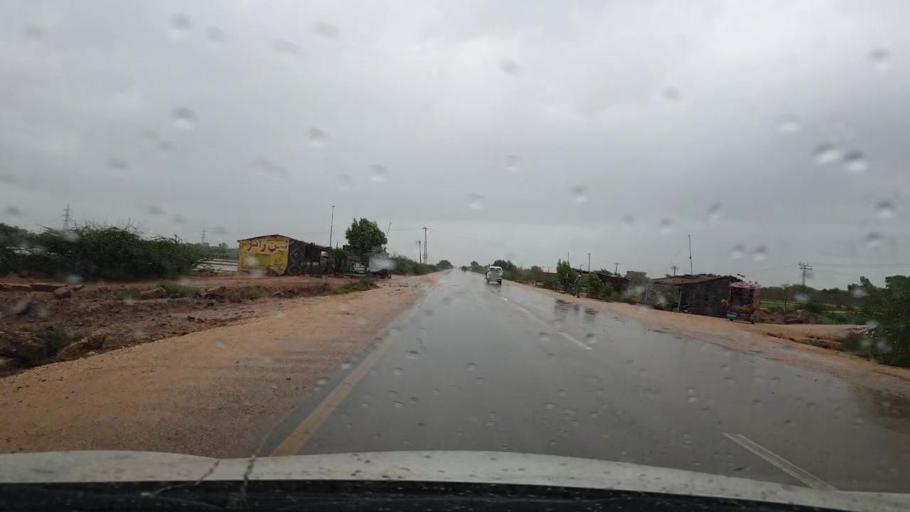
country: PK
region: Sindh
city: Kario
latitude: 24.6534
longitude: 68.5694
